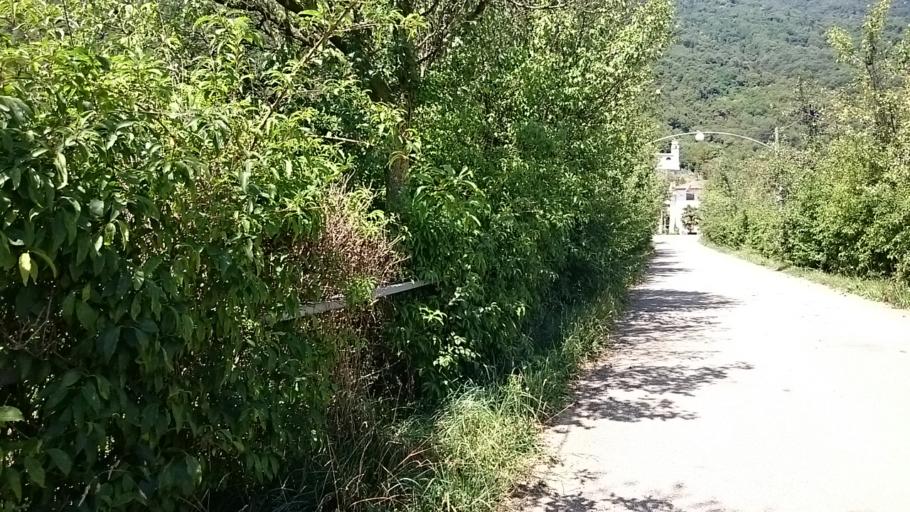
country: IT
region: Veneto
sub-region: Provincia di Treviso
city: Tarzo
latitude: 45.9777
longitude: 12.1947
